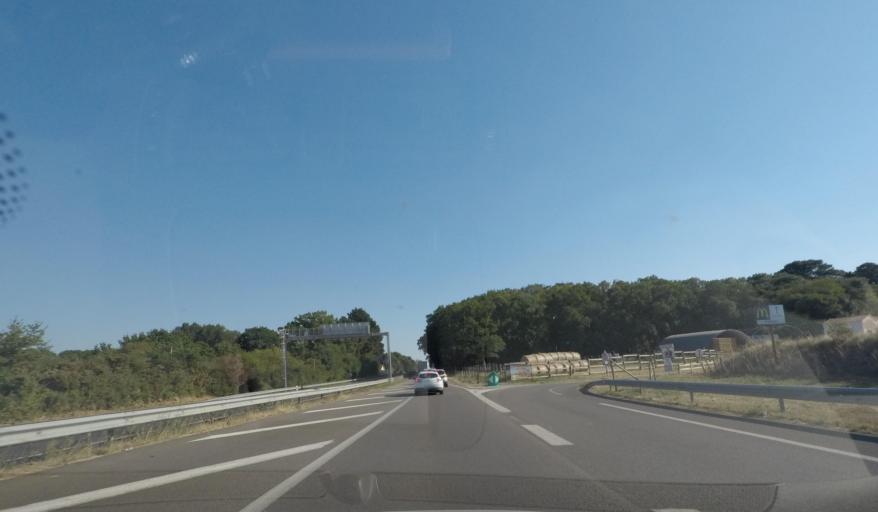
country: FR
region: Pays de la Loire
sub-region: Departement de la Loire-Atlantique
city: Saint-Michel-Chef-Chef
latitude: 47.2089
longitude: -2.1504
